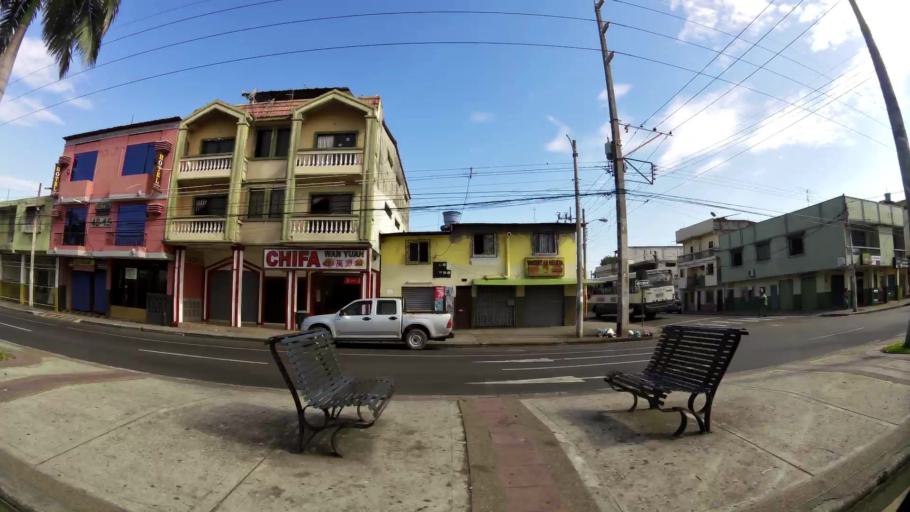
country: EC
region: Guayas
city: Guayaquil
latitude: -2.2006
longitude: -79.9207
